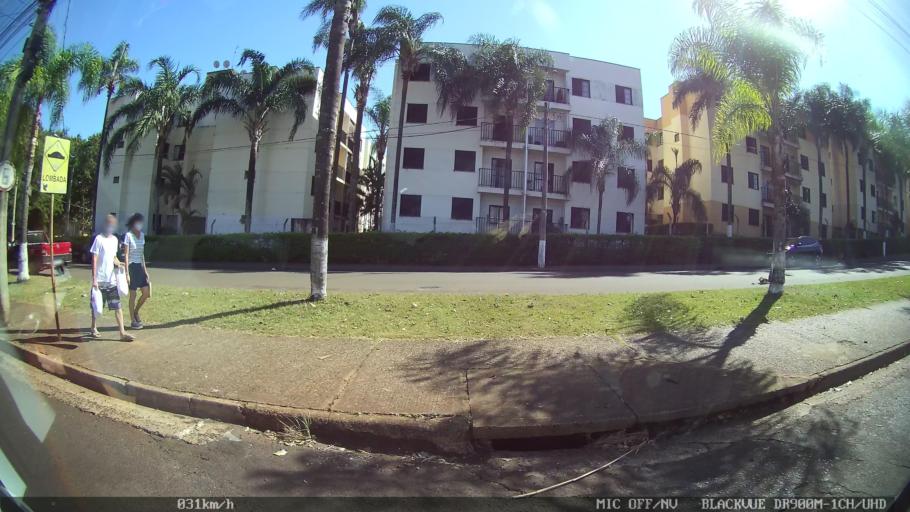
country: BR
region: Sao Paulo
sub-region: Batatais
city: Batatais
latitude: -20.8889
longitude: -47.5778
